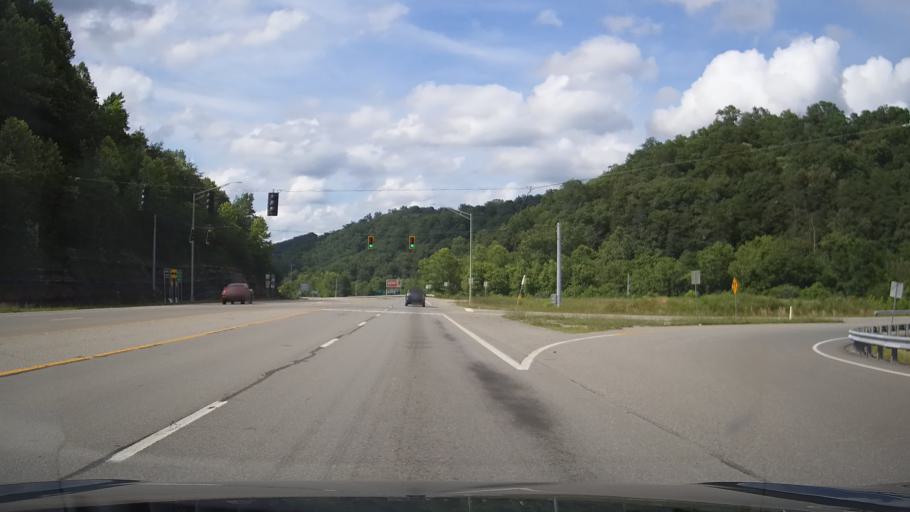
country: US
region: Kentucky
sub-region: Johnson County
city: Van Lear
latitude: 37.7228
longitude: -82.7877
